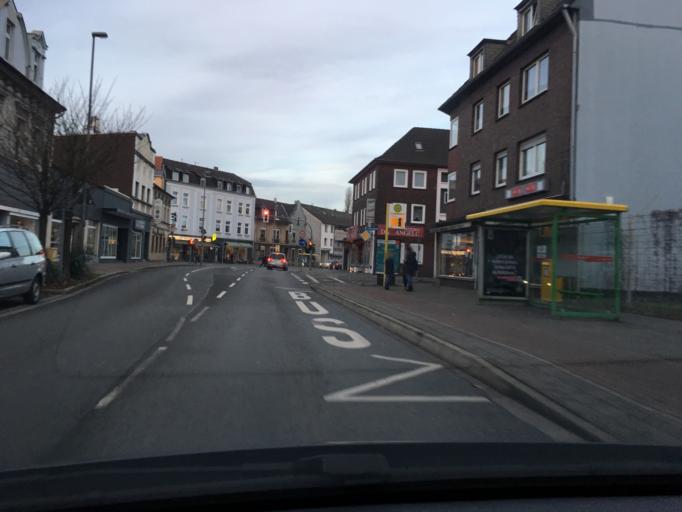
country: DE
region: North Rhine-Westphalia
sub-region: Regierungsbezirk Dusseldorf
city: Oberhausen
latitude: 51.4622
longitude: 6.8344
